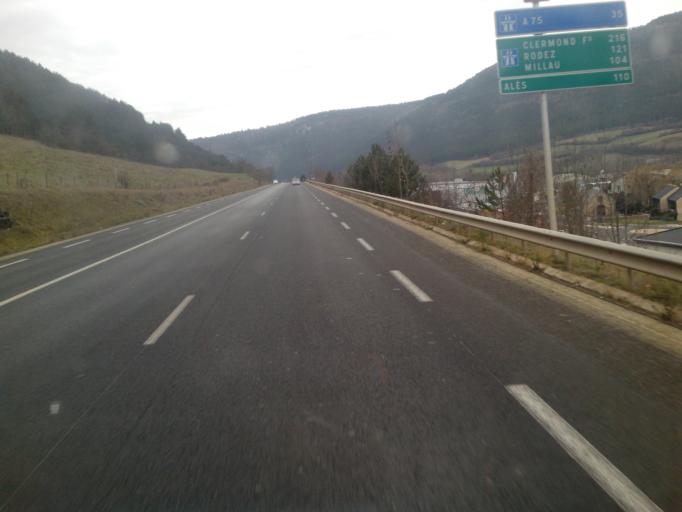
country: FR
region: Languedoc-Roussillon
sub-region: Departement de la Lozere
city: Mende
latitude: 44.5150
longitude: 3.4805
